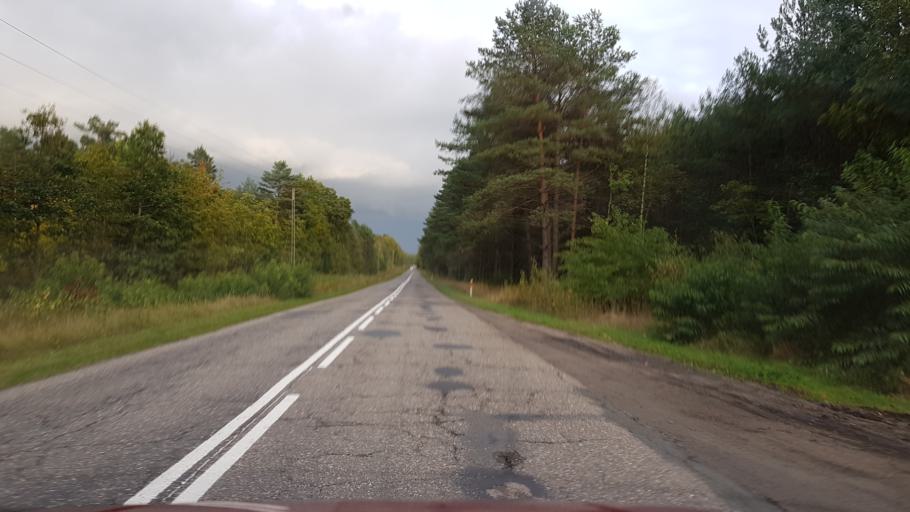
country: PL
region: West Pomeranian Voivodeship
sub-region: Powiat walecki
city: Tuczno
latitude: 53.1719
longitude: 16.3105
